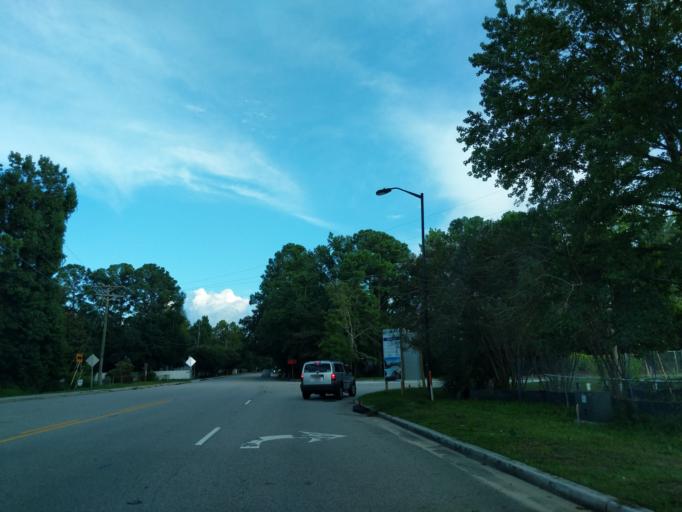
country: US
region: South Carolina
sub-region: Charleston County
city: Isle of Palms
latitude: 32.8390
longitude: -79.8145
